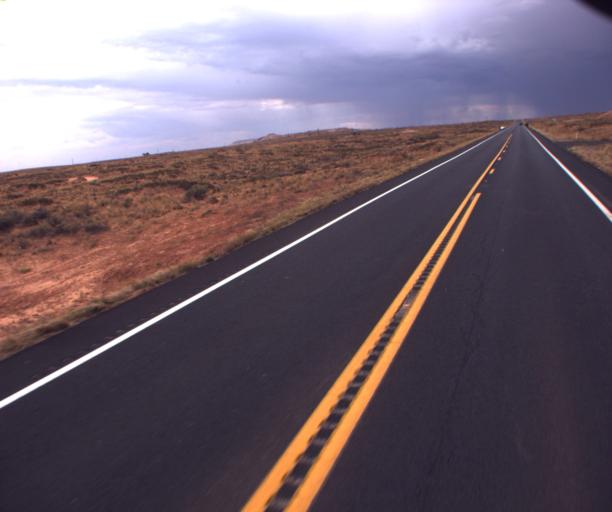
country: US
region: Arizona
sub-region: Coconino County
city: Kaibito
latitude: 36.3049
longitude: -110.9701
